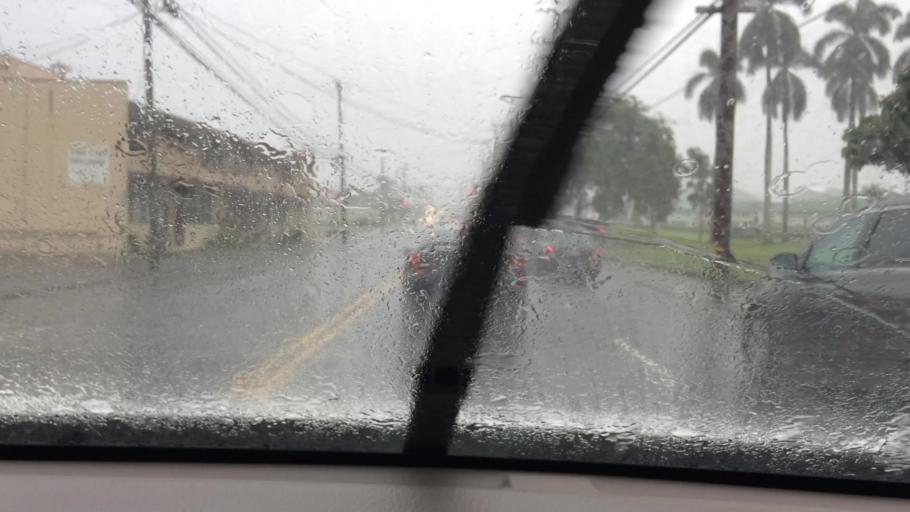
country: US
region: Hawaii
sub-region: Hawaii County
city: Hilo
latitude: 19.7154
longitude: -155.0779
